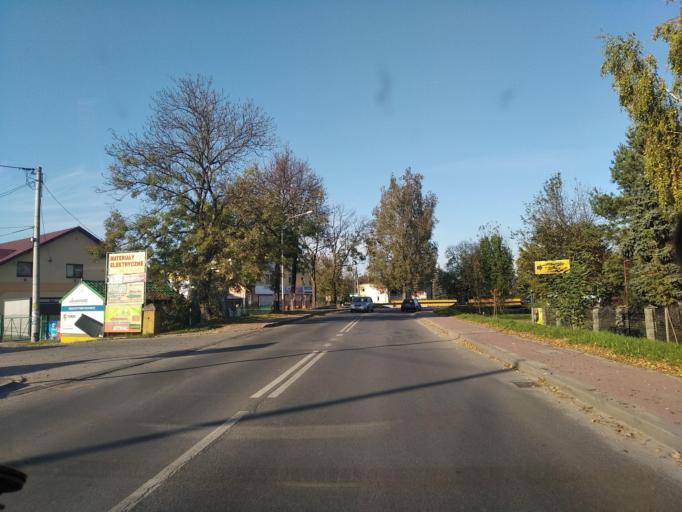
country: PL
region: Subcarpathian Voivodeship
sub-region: Powiat brzozowski
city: Brzozow
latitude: 49.7003
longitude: 22.0191
